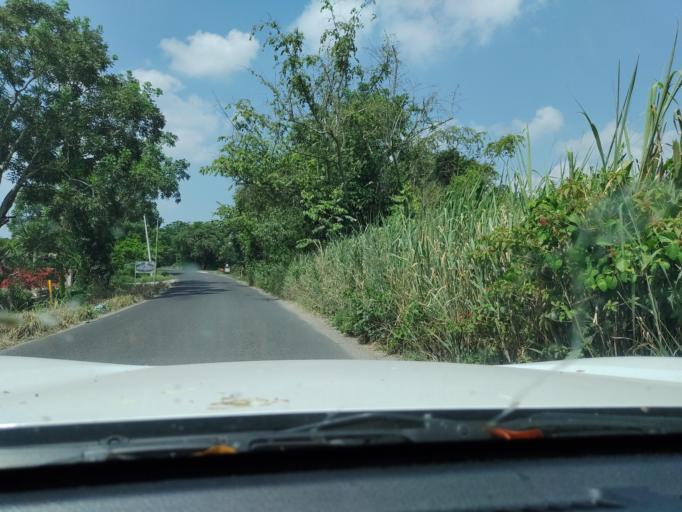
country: MX
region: Veracruz
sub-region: Atzalan
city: Colonias Pedernales
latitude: 20.0584
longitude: -97.0259
